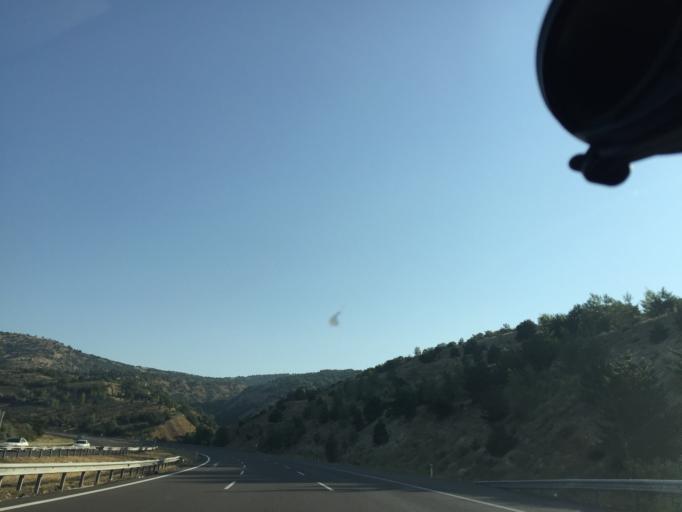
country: TR
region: Ankara
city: Celtikci
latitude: 40.3734
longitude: 32.4706
